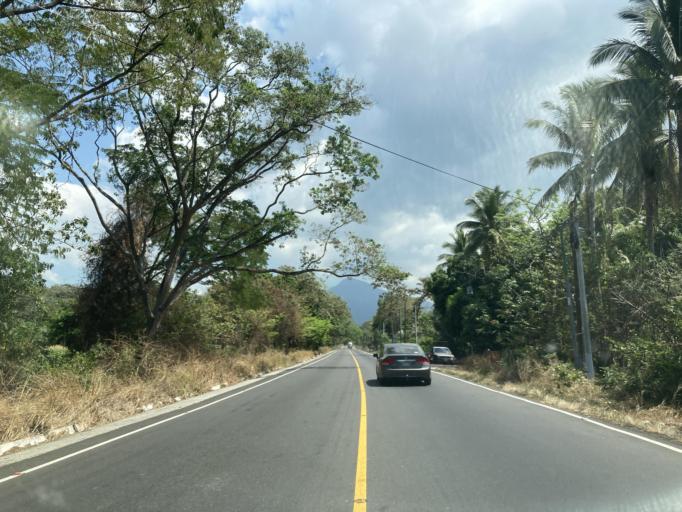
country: GT
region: Santa Rosa
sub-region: Municipio de Taxisco
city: Taxisco
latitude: 14.0988
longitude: -90.5379
